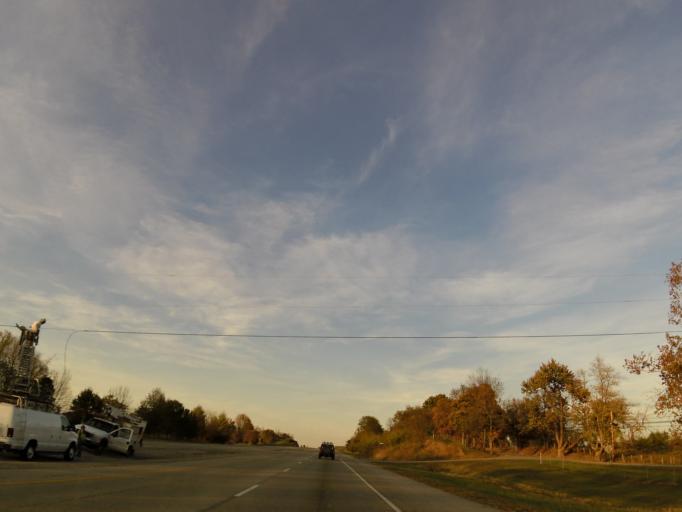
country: US
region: Kentucky
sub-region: Jessamine County
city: Wilmore
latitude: 37.7919
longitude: -84.6047
